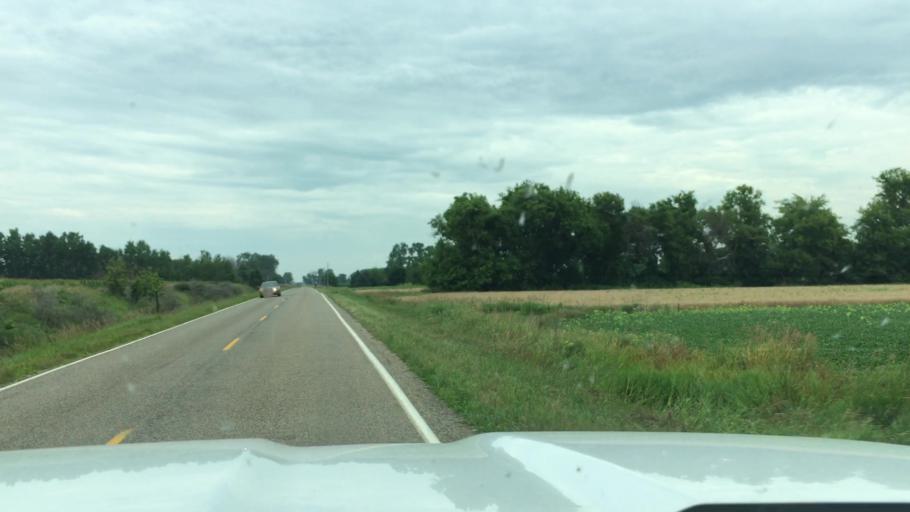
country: US
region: Michigan
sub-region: Clinton County
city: Saint Johns
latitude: 43.0537
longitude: -84.4841
